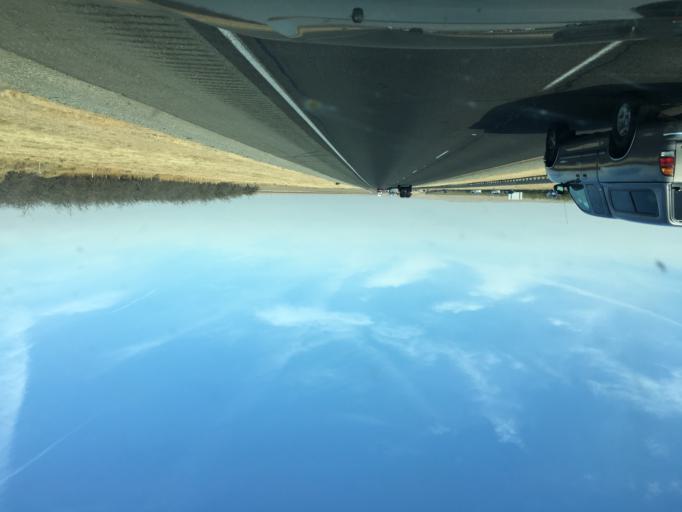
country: US
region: California
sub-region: Fresno County
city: San Joaquin
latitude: 36.4483
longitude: -120.4051
